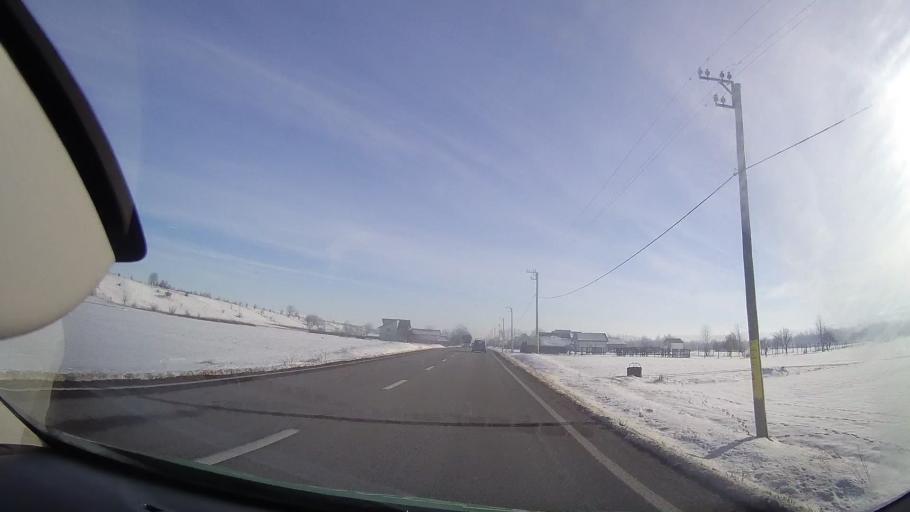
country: RO
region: Neamt
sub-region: Comuna Ghindaoani
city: Ghindaoani
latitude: 47.0847
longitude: 26.3365
